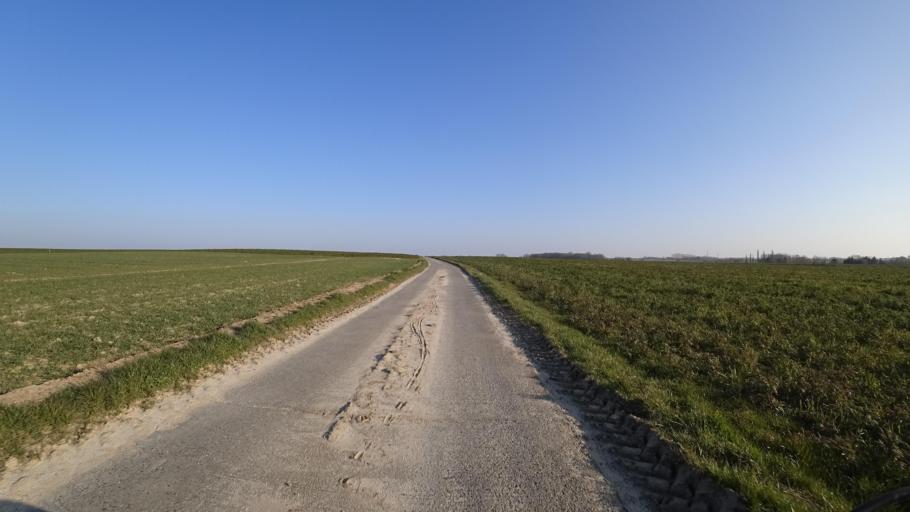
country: BE
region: Wallonia
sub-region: Province du Brabant Wallon
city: Chastre
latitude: 50.5757
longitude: 4.6573
